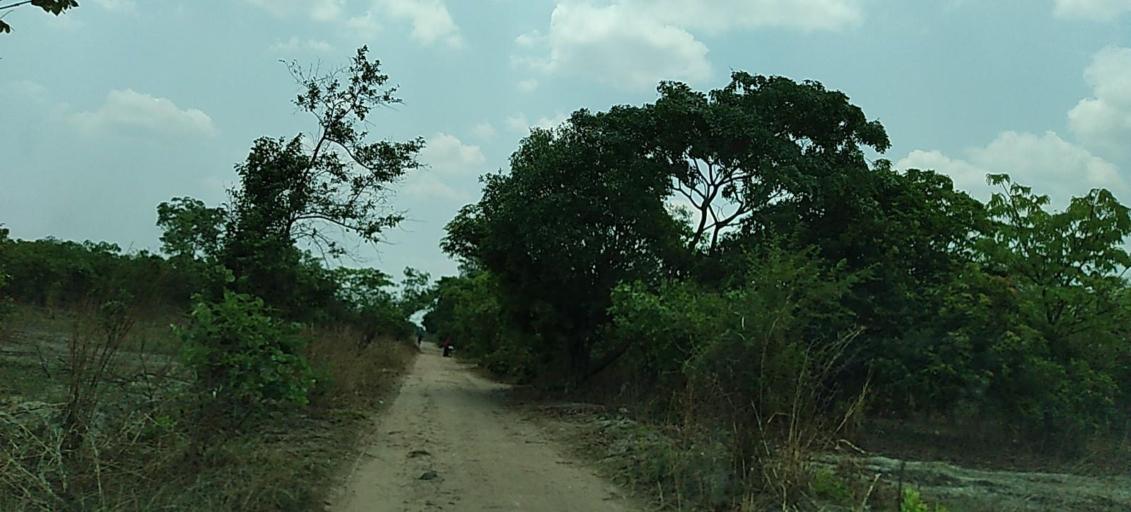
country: ZM
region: Copperbelt
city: Luanshya
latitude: -13.0995
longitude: 28.2988
